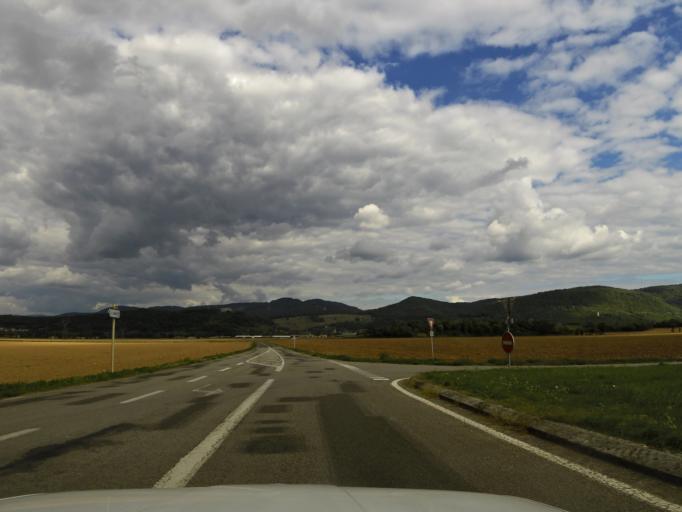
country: FR
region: Rhone-Alpes
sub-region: Departement de l'Ain
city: Saint-Denis-en-Bugey
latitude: 45.9226
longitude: 5.3227
